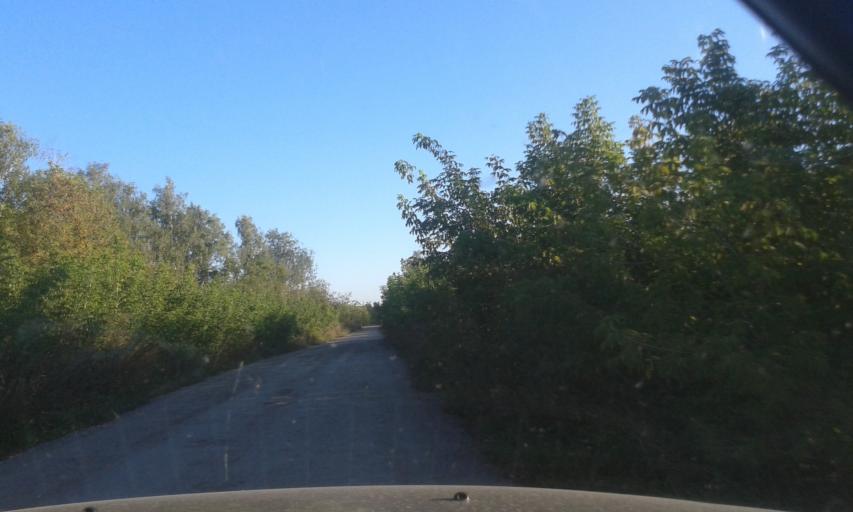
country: RU
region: Tula
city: Krapivna
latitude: 54.1331
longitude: 37.1571
